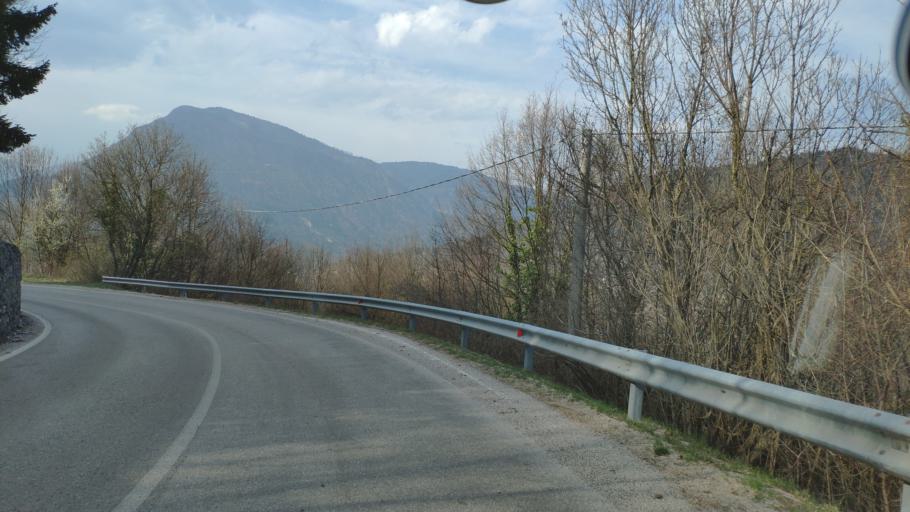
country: IT
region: Veneto
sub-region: Provincia di Vicenza
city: Enego
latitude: 45.9464
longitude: 11.7209
